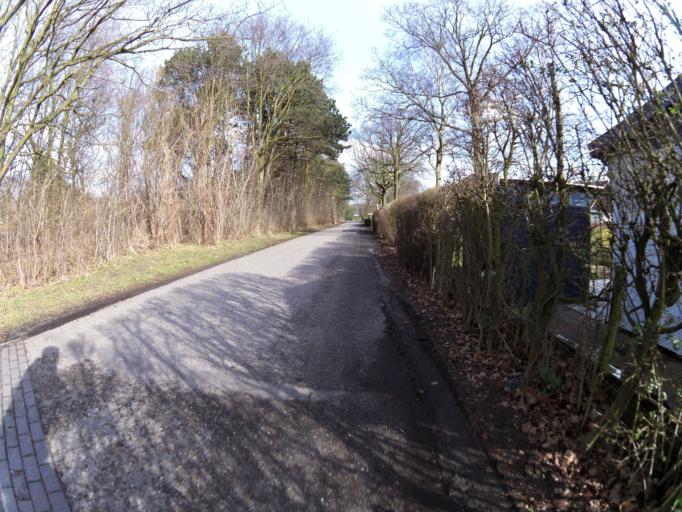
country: NL
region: South Holland
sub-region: Gemeente Brielle
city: Brielle
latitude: 51.9249
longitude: 4.1245
